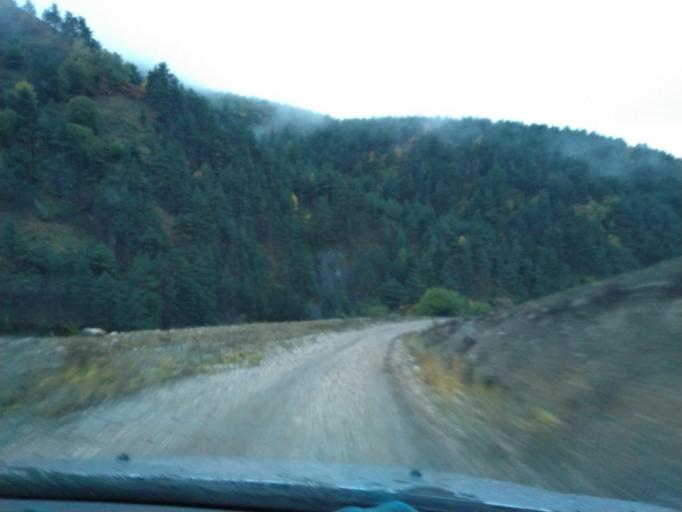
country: RU
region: North Ossetia
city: Tarskoye
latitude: 42.8240
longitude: 44.9745
